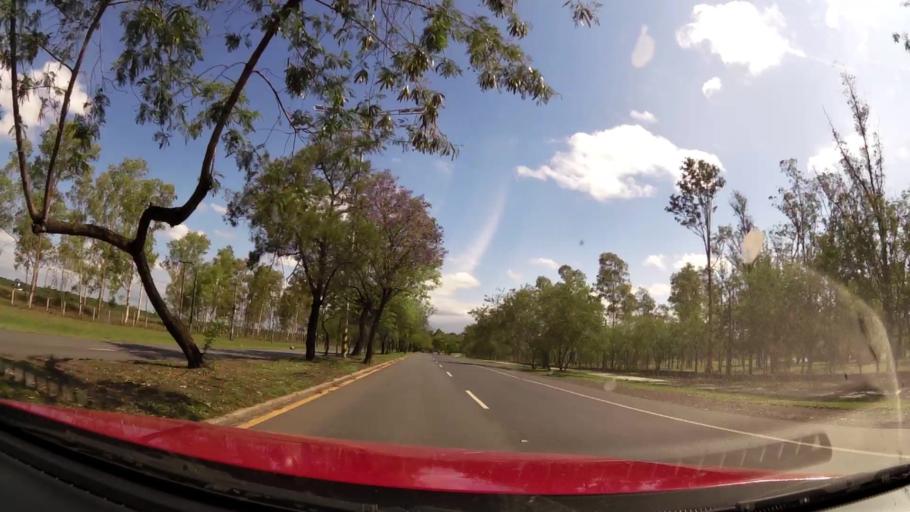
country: PY
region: Central
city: Fernando de la Mora
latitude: -25.2693
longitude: -57.5375
